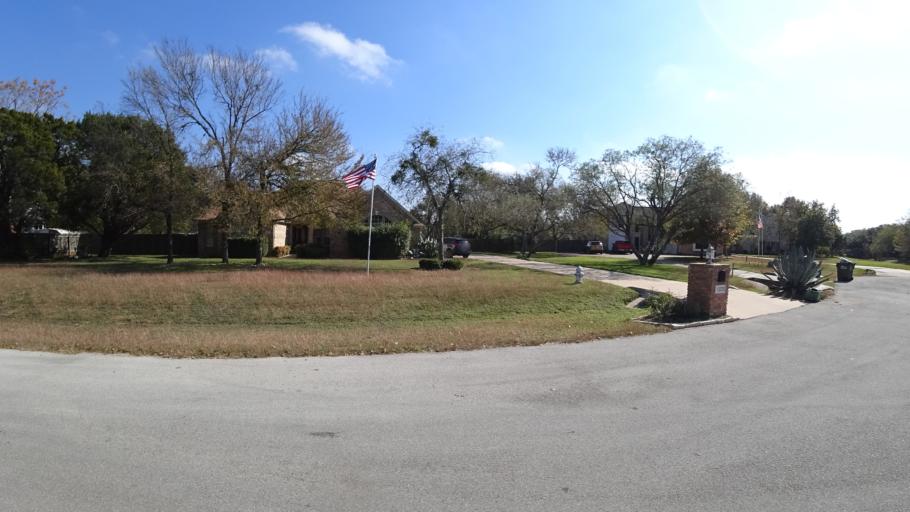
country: US
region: Texas
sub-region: Travis County
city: Shady Hollow
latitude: 30.1601
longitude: -97.8612
